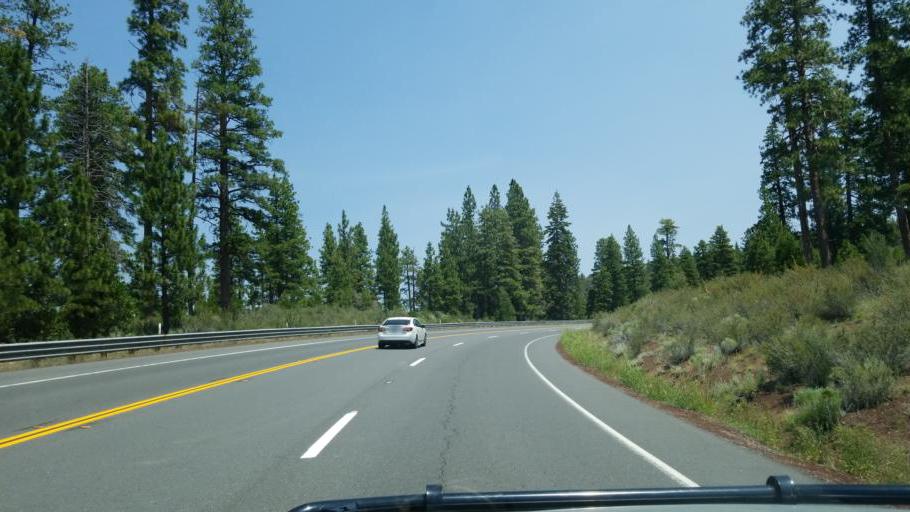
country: US
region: California
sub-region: Shasta County
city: Burney
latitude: 40.7024
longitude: -121.3996
